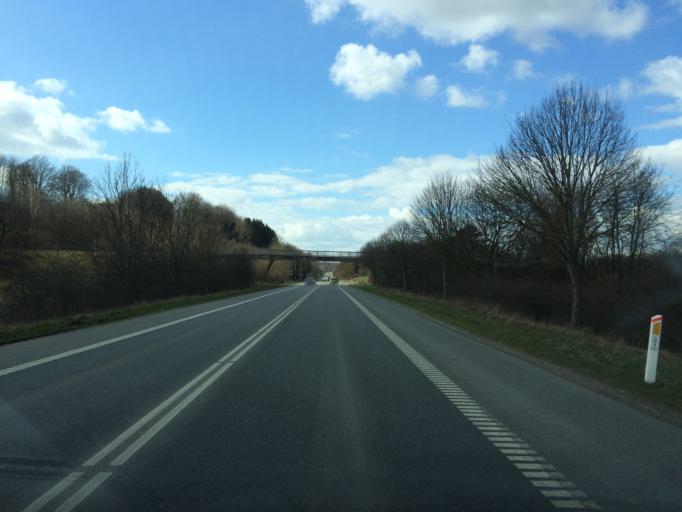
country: DK
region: South Denmark
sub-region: Assens Kommune
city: Vissenbjerg
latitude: 55.3901
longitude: 10.1324
